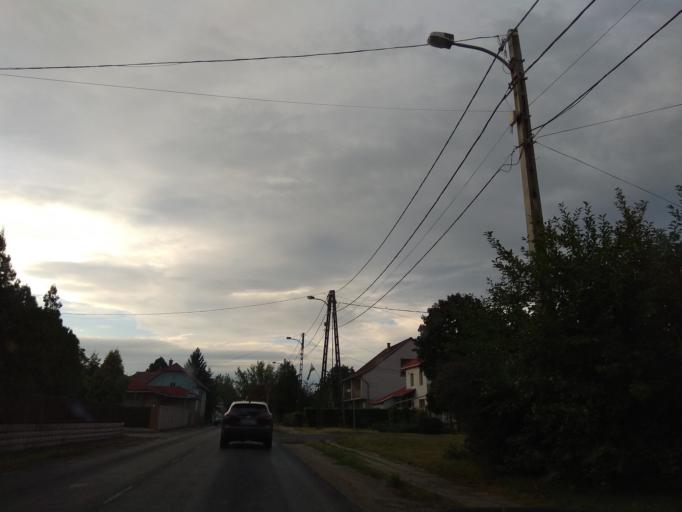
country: HU
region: Borsod-Abauj-Zemplen
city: Miskolc
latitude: 48.0933
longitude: 20.8060
